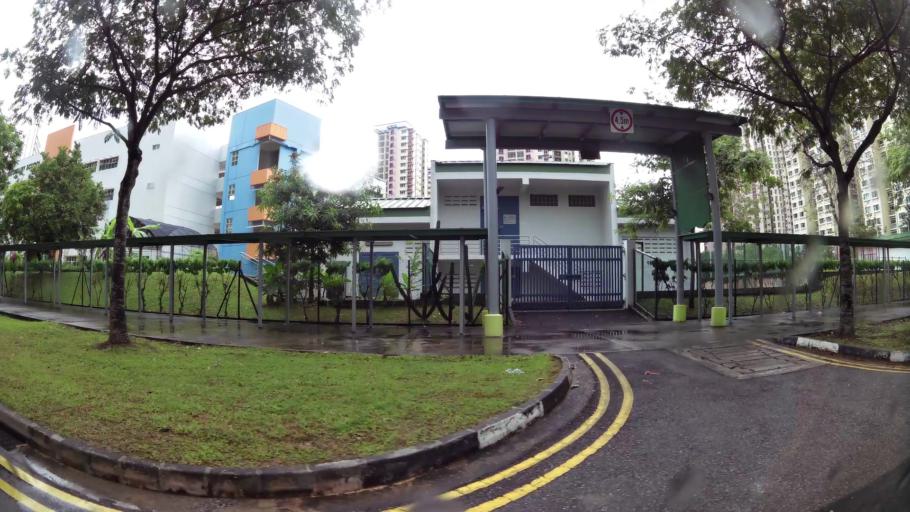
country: MY
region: Johor
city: Kampung Pasir Gudang Baru
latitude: 1.3912
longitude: 103.8776
